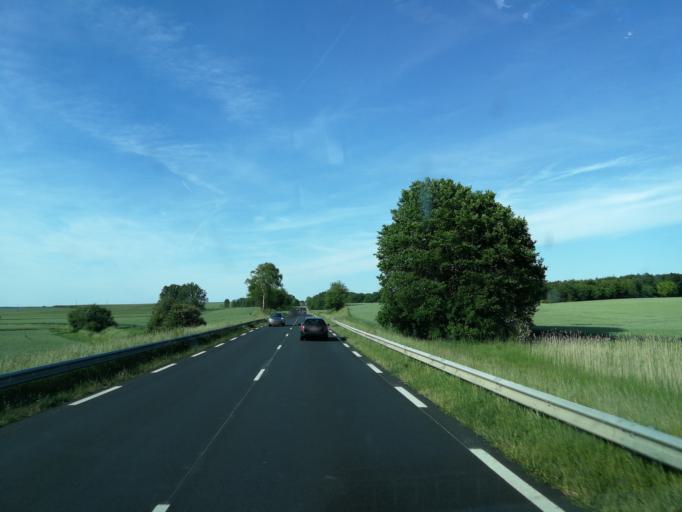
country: FR
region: Centre
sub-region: Departement du Loir-et-Cher
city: Saint-Amand-Longpre
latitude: 47.7216
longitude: 1.0202
